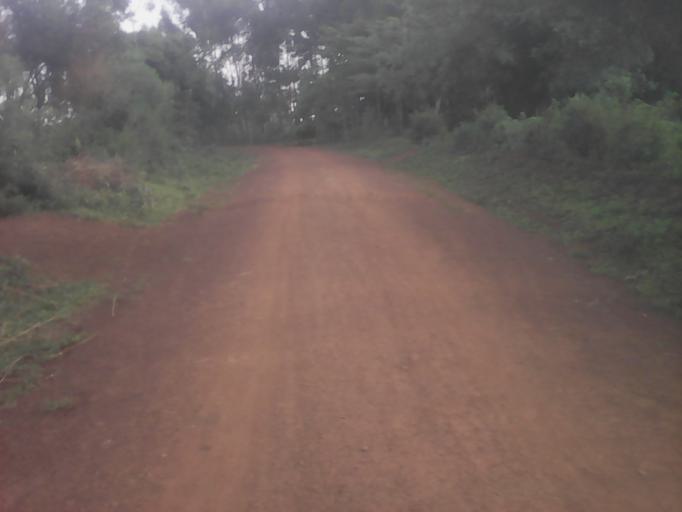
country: UG
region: Eastern Region
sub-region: Busia District
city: Busia
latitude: 0.5317
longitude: 34.0370
